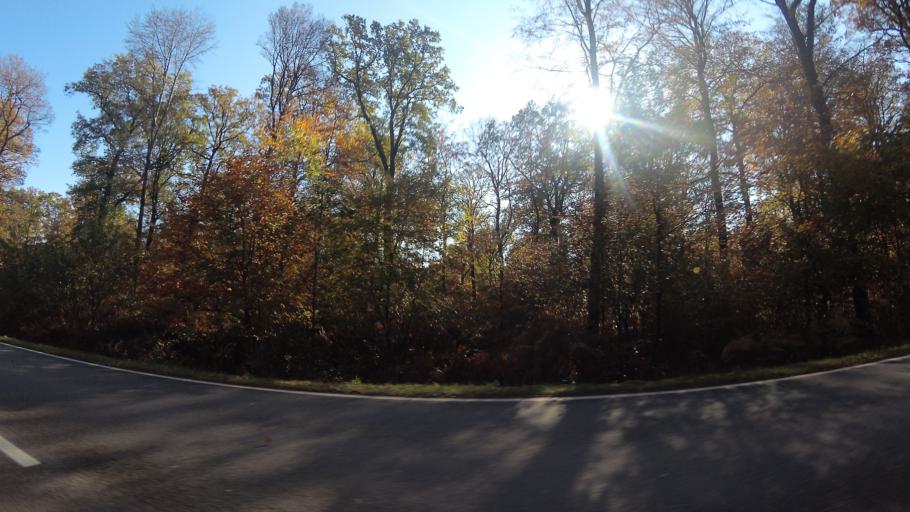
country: DE
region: Saarland
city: Weiskirchen
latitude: 49.5418
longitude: 6.8477
